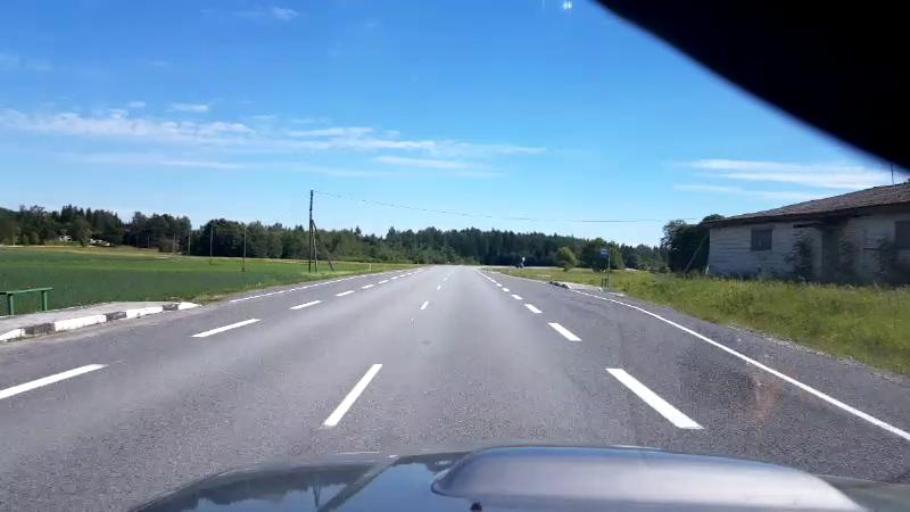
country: EE
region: Jaervamaa
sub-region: Jaerva-Jaani vald
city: Jarva-Jaani
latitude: 59.0017
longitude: 25.9345
